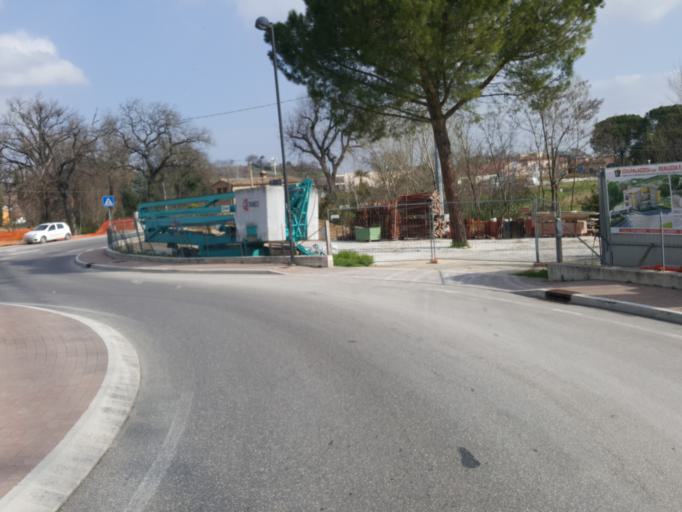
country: IT
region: The Marches
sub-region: Provincia di Macerata
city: Passo di Treia
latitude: 43.2866
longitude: 13.3327
